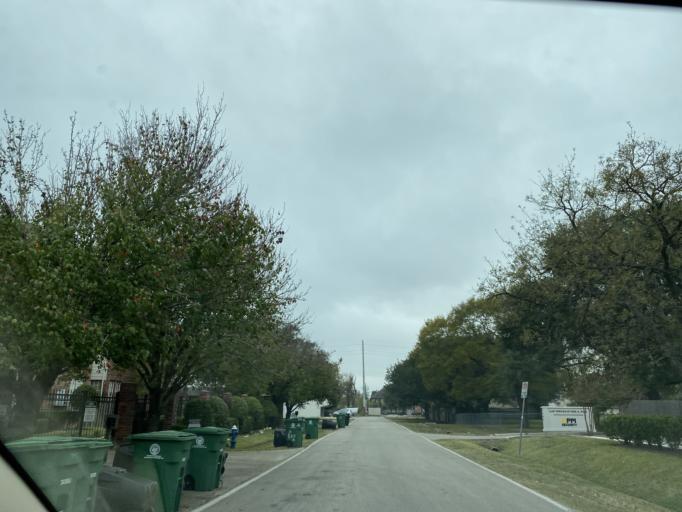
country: US
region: Texas
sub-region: Harris County
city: Bellaire
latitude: 29.7343
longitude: -95.4826
